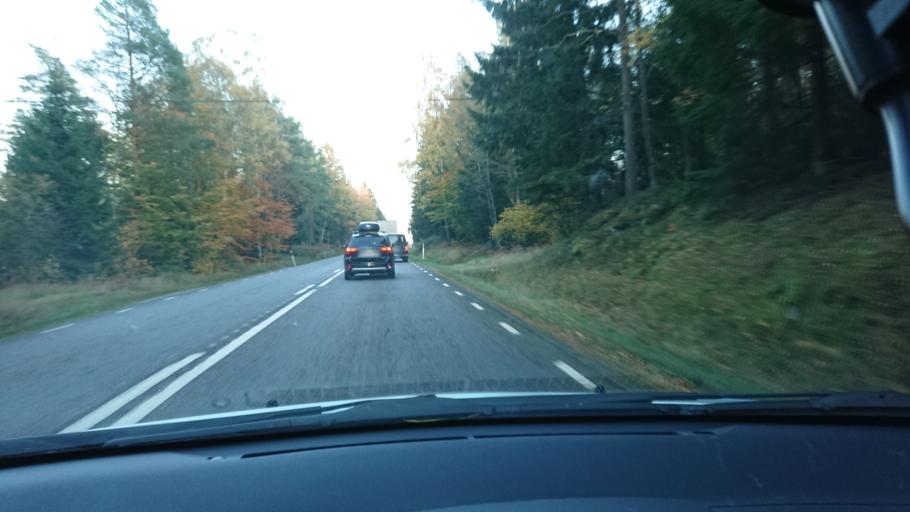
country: SE
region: Halland
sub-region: Laholms Kommun
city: Veinge
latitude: 56.7192
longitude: 13.1783
